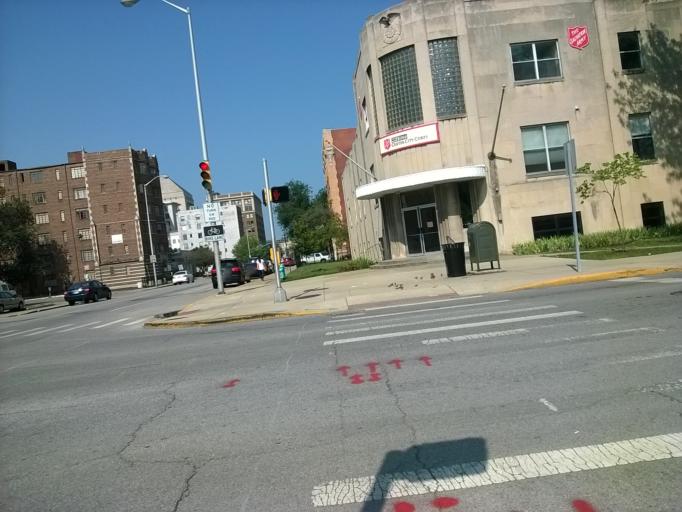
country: US
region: Indiana
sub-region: Marion County
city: Indianapolis
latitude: 39.7741
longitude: -86.1523
